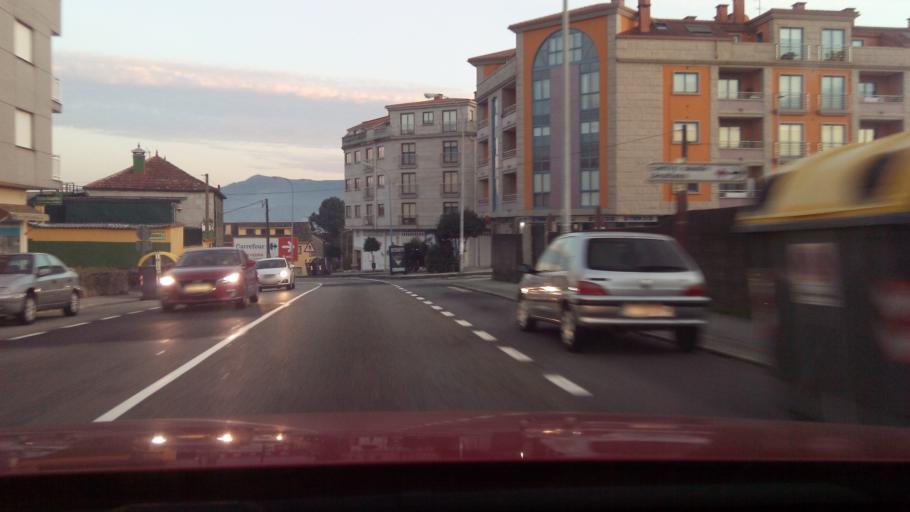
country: ES
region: Galicia
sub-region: Provincia de Pontevedra
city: Poio
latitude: 42.4318
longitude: -8.6659
